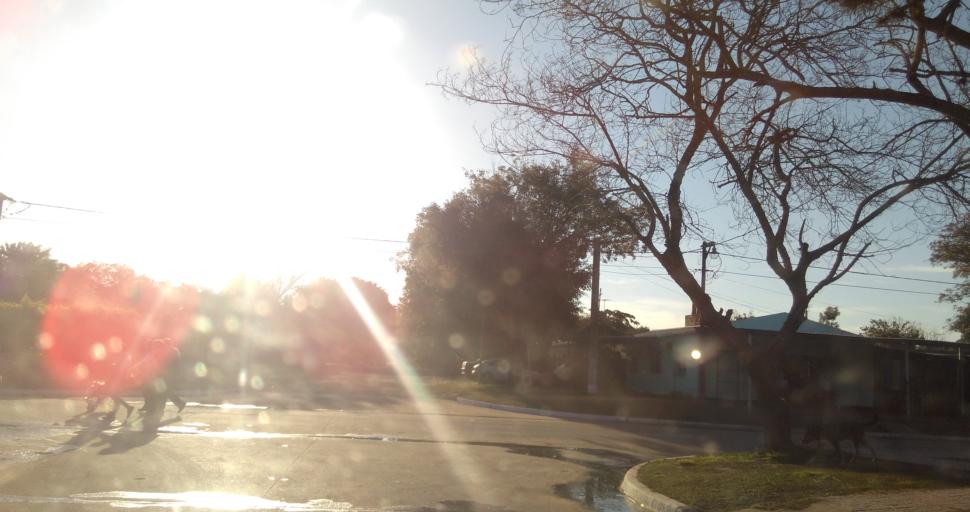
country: AR
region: Chaco
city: Colonia Benitez
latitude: -27.3319
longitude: -58.9456
